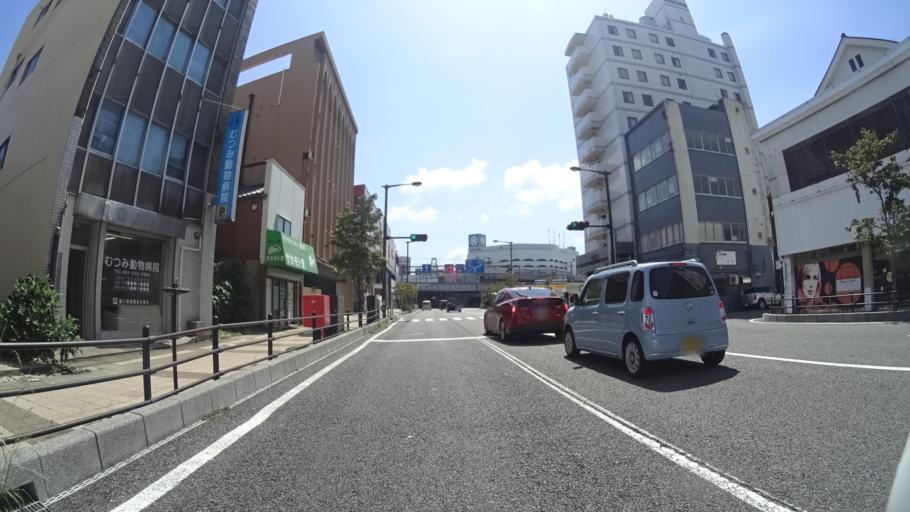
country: JP
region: Yamaguchi
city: Shimonoseki
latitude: 33.9521
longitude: 130.9218
